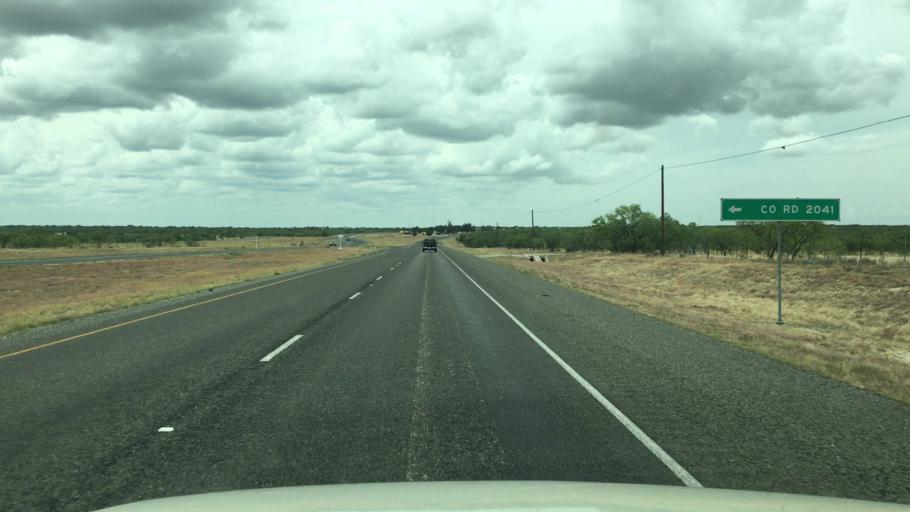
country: US
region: Texas
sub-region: Concho County
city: Eden
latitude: 31.2175
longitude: -99.9518
